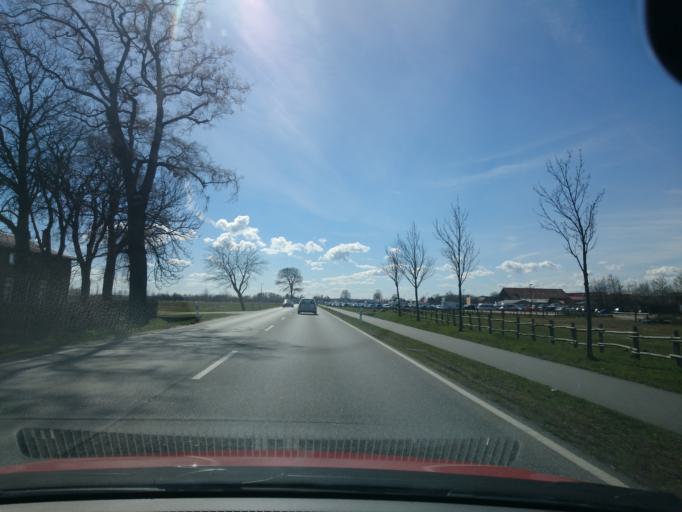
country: DE
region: Mecklenburg-Vorpommern
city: Rovershagen
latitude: 54.1636
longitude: 12.2359
